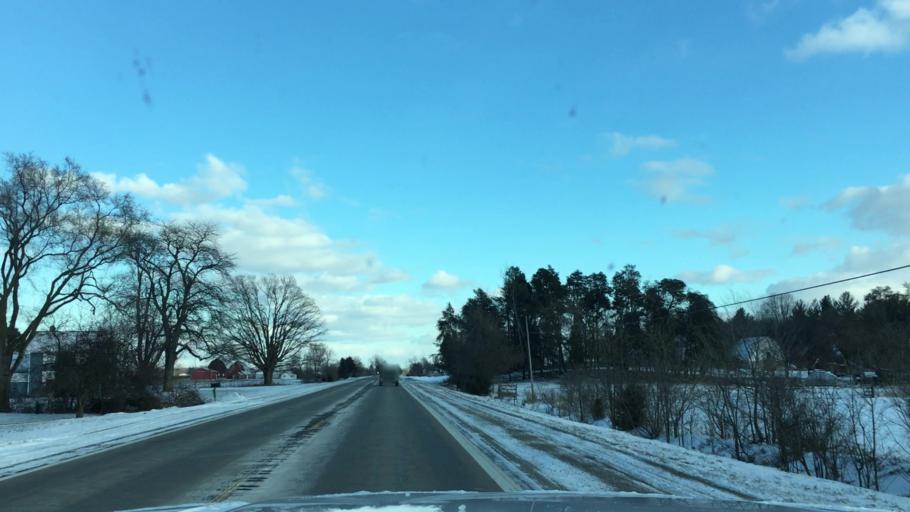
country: US
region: Michigan
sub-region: Saginaw County
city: Chesaning
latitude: 43.1869
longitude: -84.2002
